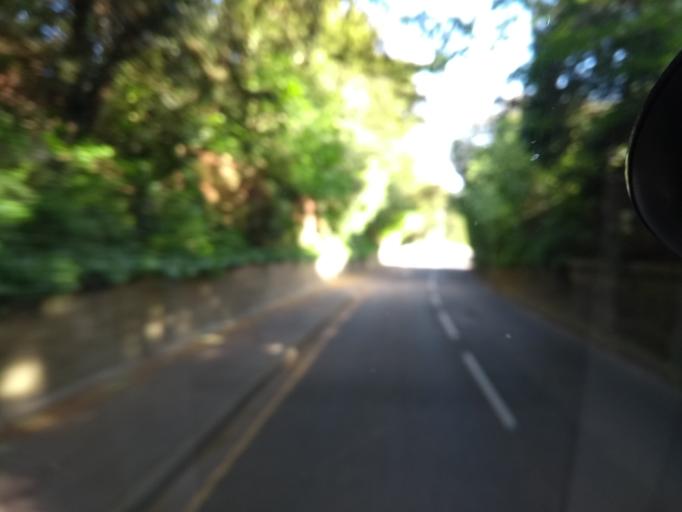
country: GB
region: England
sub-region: Somerset
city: Taunton
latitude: 51.0099
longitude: -3.1107
